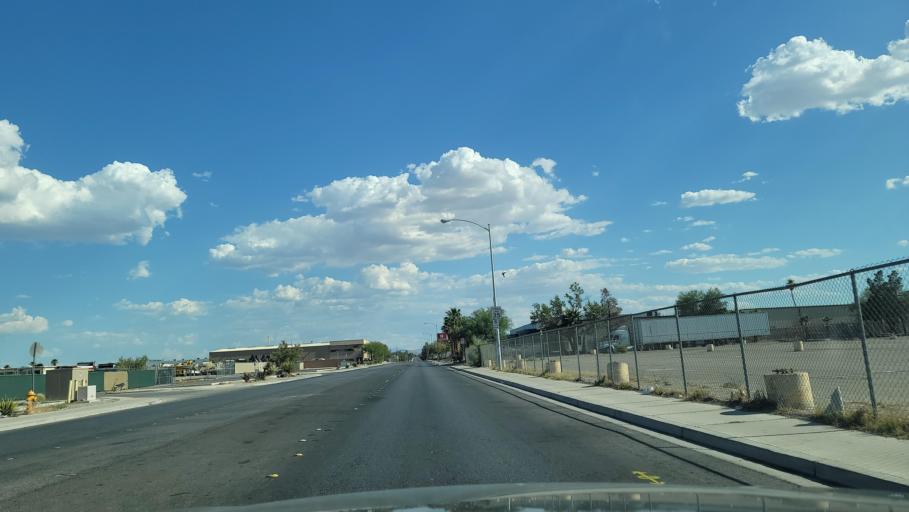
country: US
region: Nevada
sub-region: Clark County
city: Spring Valley
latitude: 36.1000
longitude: -115.2040
